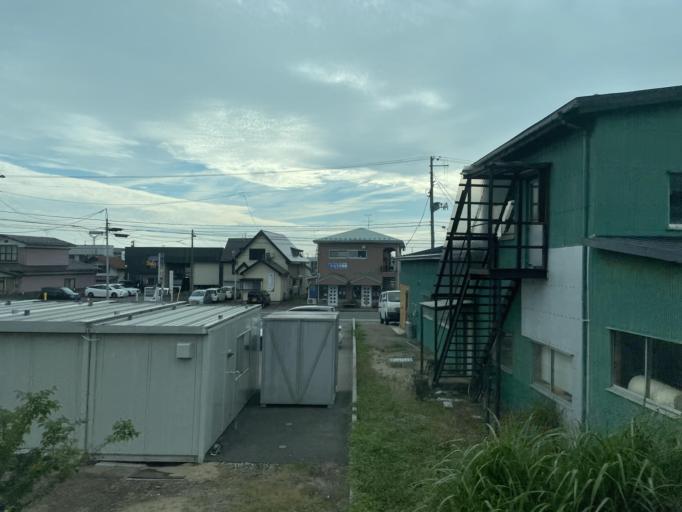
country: JP
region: Akita
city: Akita Shi
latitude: 39.7730
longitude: 140.0703
